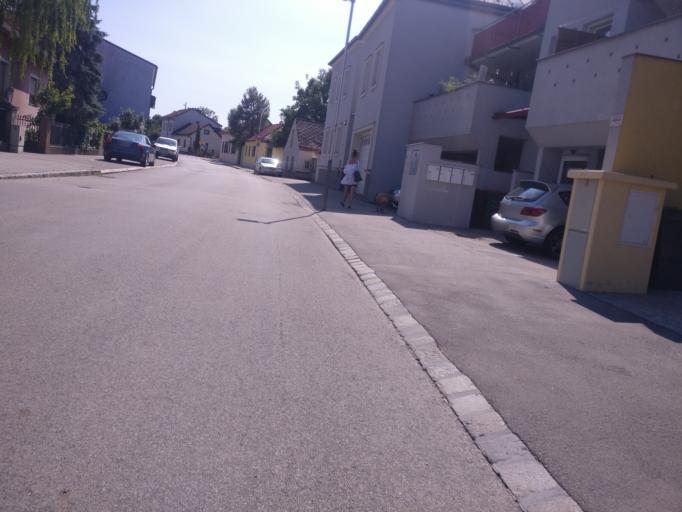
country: AT
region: Lower Austria
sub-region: Politischer Bezirk Modling
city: Guntramsdorf
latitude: 48.0450
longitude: 16.3120
